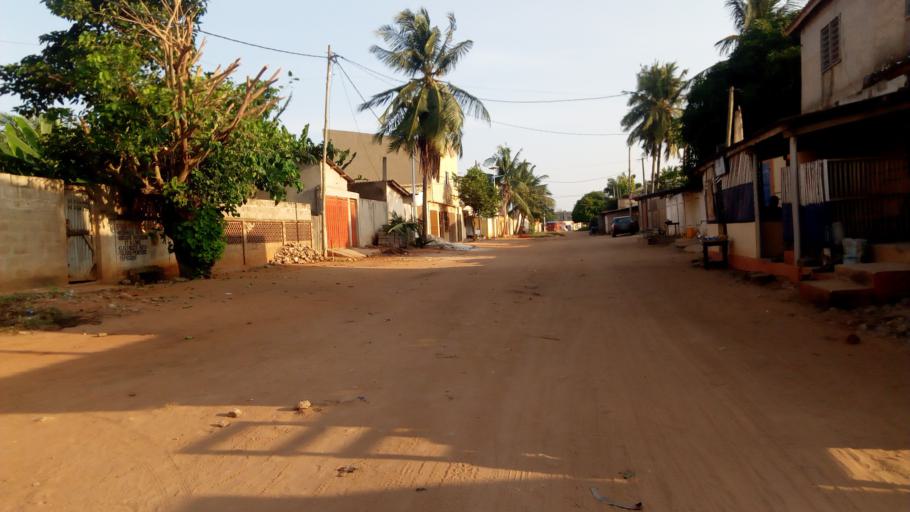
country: TG
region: Maritime
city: Lome
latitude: 6.1789
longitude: 1.1905
